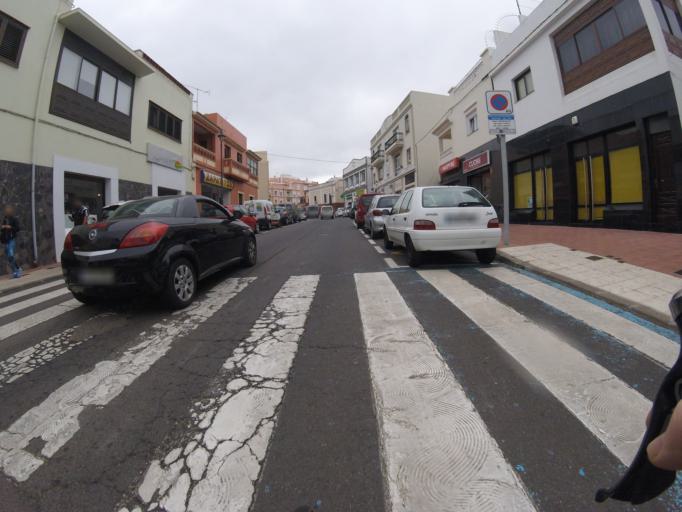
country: ES
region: Canary Islands
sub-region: Provincia de Santa Cruz de Tenerife
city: Tegueste
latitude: 28.5334
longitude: -16.3619
